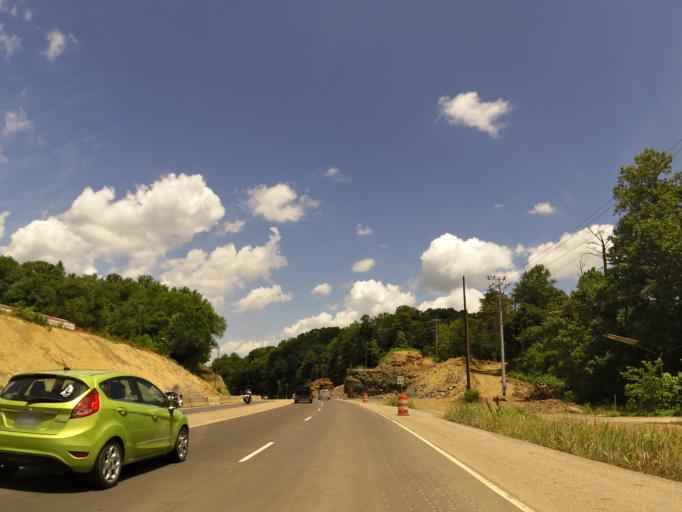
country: US
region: Tennessee
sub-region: Union County
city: Condon
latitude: 36.1487
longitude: -83.9122
